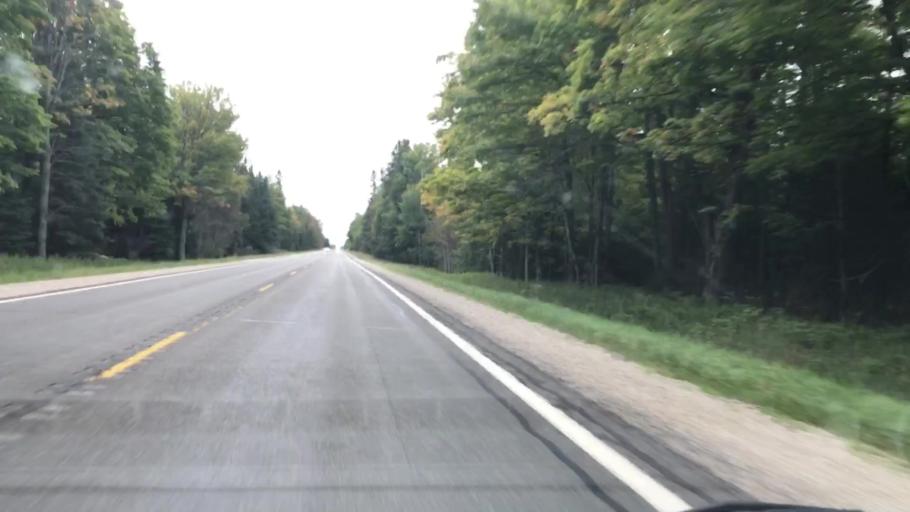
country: US
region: Michigan
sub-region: Luce County
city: Newberry
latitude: 46.2271
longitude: -85.5721
